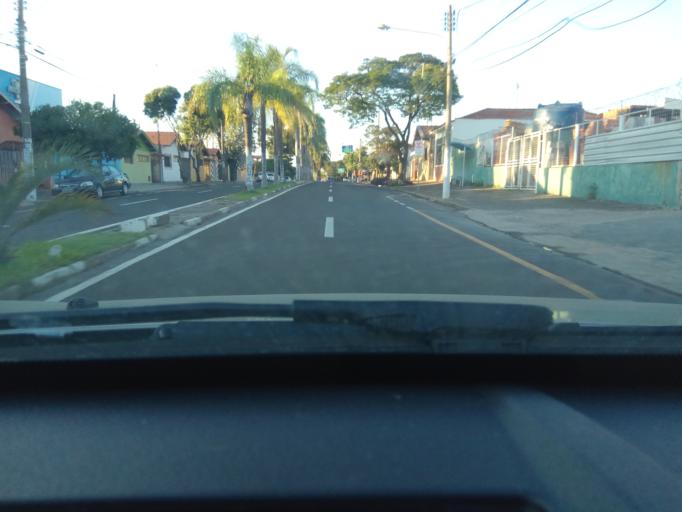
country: BR
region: Sao Paulo
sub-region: Piracicaba
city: Piracicaba
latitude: -22.7362
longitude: -47.6640
